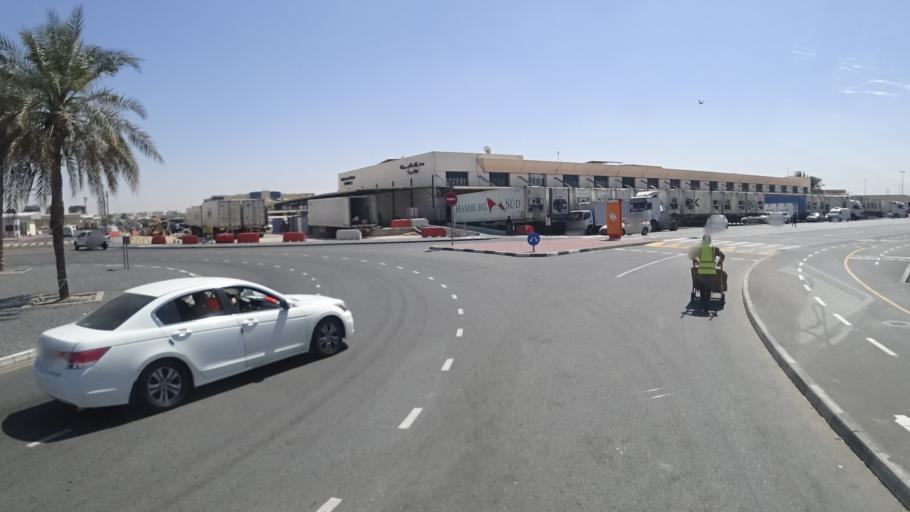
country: AE
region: Ash Shariqah
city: Sharjah
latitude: 25.1756
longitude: 55.3881
